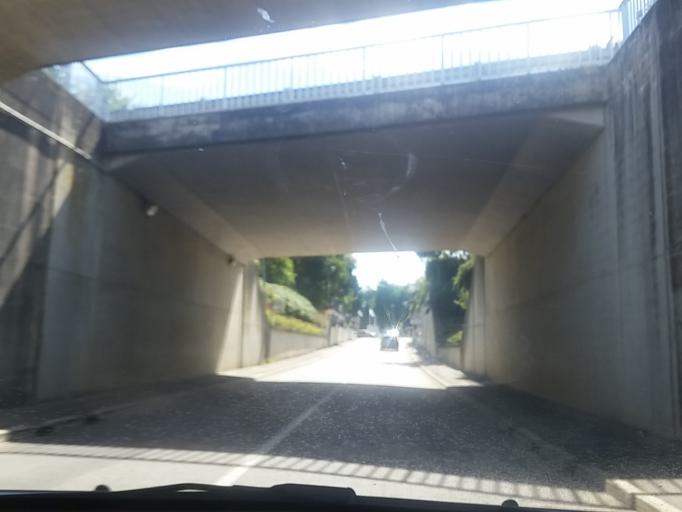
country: FR
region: Pays de la Loire
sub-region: Departement de la Loire-Atlantique
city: Saint-Michel-Chef-Chef
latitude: 47.1836
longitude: -2.1460
